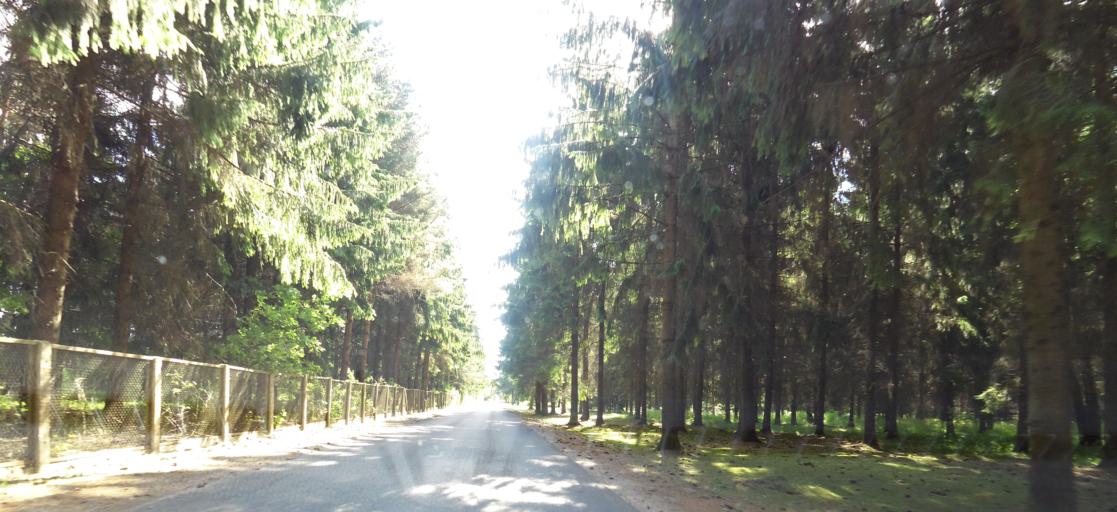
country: LT
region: Panevezys
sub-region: Birzai
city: Birzai
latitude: 56.1872
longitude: 24.7577
